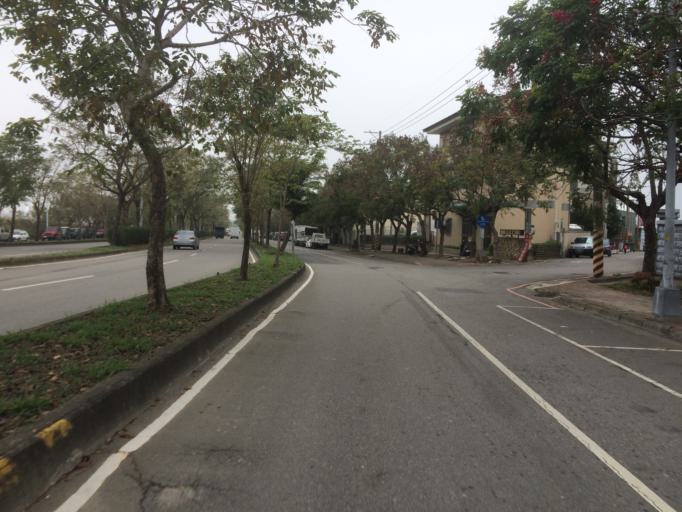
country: TW
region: Taiwan
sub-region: Taichung City
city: Taichung
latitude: 24.1613
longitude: 120.7375
